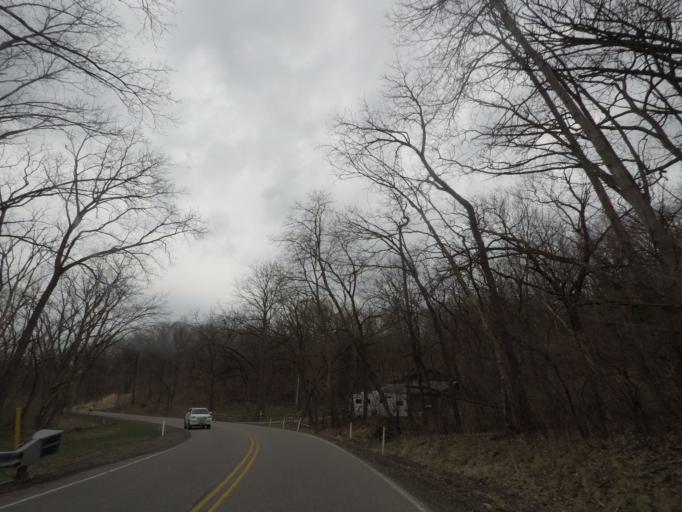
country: US
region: Wisconsin
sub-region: Dane County
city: Cross Plains
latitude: 43.1069
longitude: -89.5904
